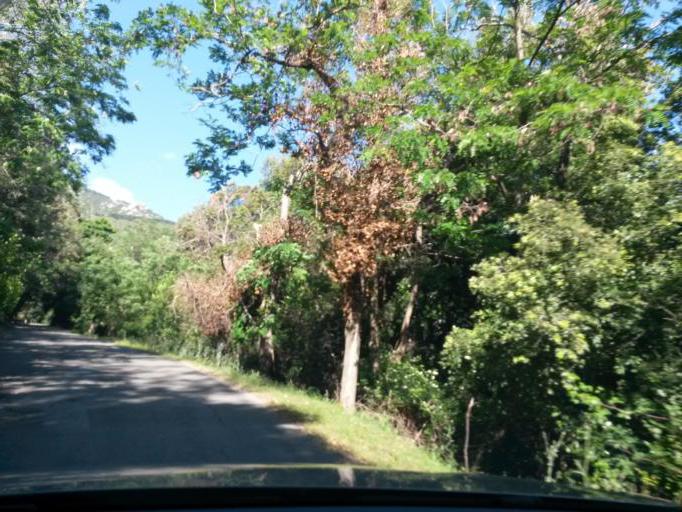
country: IT
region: Tuscany
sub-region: Provincia di Livorno
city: Marciana
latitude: 42.7920
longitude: 10.1779
